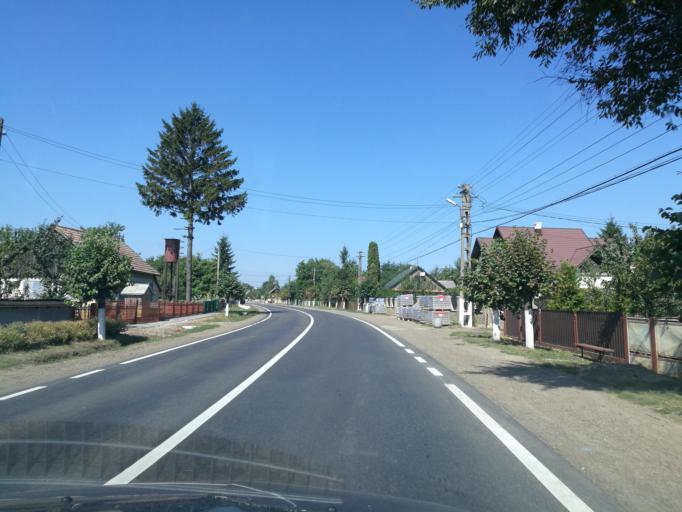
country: RO
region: Suceava
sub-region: Comuna Milisauti
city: Badeuti
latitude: 47.8009
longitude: 25.9890
